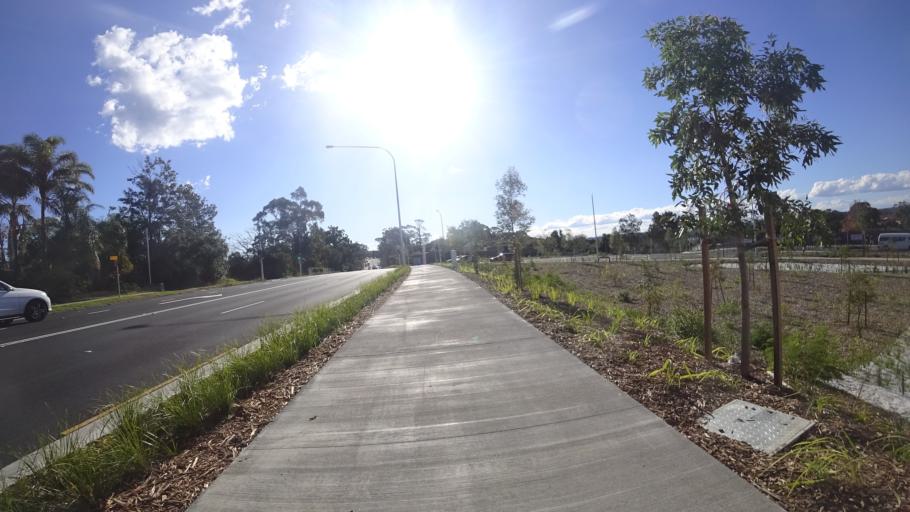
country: AU
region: New South Wales
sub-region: The Hills Shire
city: West Pennant
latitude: -33.7362
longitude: 151.0309
